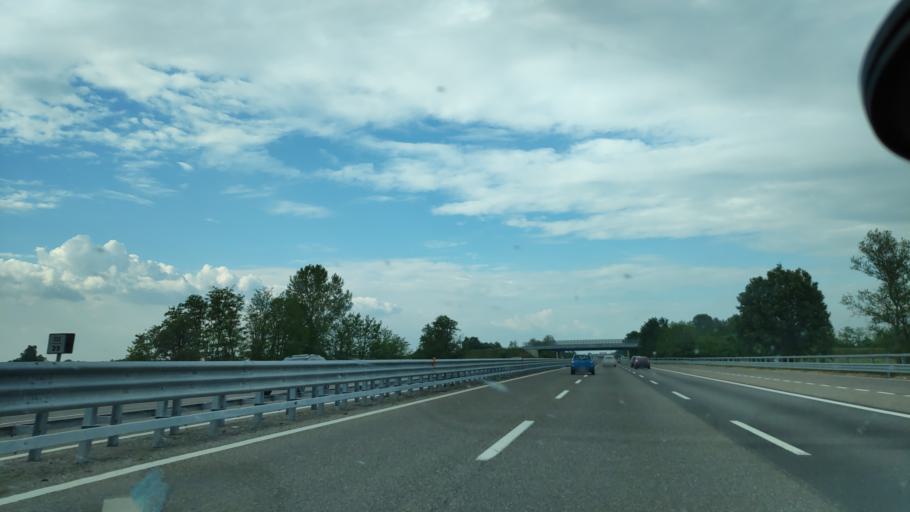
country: IT
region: Lombardy
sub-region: Provincia di Pavia
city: Pieve Albignola
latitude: 45.1348
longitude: 8.9834
